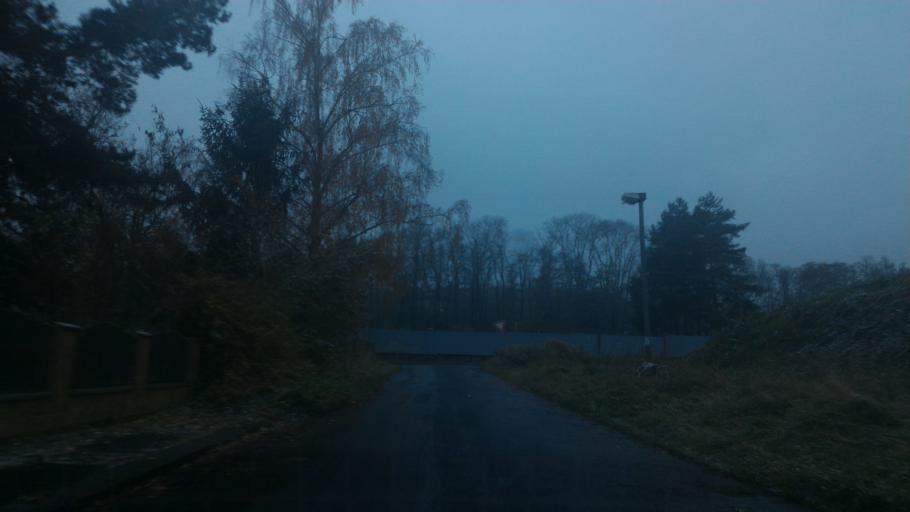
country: CZ
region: Ustecky
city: Varnsdorf
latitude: 50.9115
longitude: 14.6136
